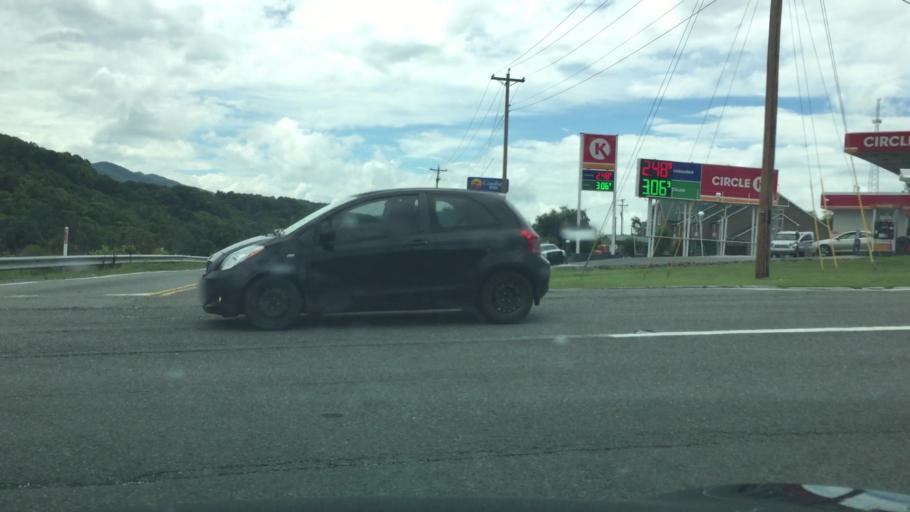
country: US
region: Virginia
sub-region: Wythe County
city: Wytheville
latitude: 36.9467
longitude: -80.9498
